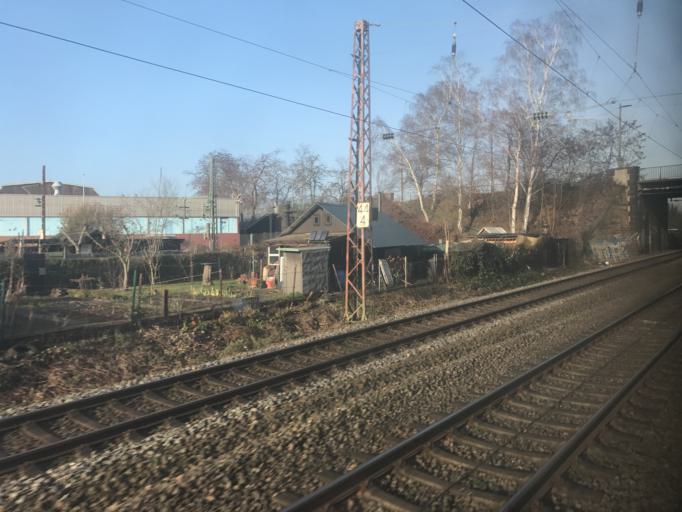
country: DE
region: North Rhine-Westphalia
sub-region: Regierungsbezirk Dusseldorf
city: Dusseldorf
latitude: 51.2621
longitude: 6.7914
